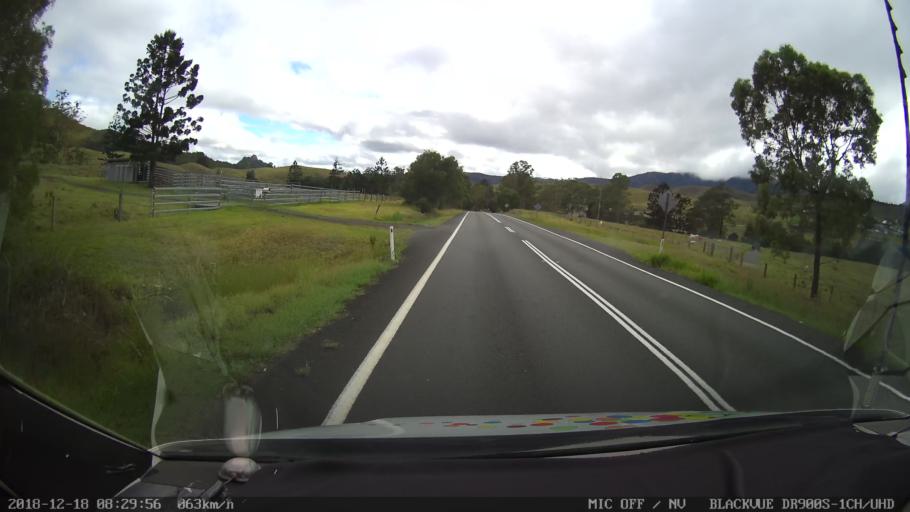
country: AU
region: New South Wales
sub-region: Kyogle
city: Kyogle
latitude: -28.3239
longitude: 152.7638
